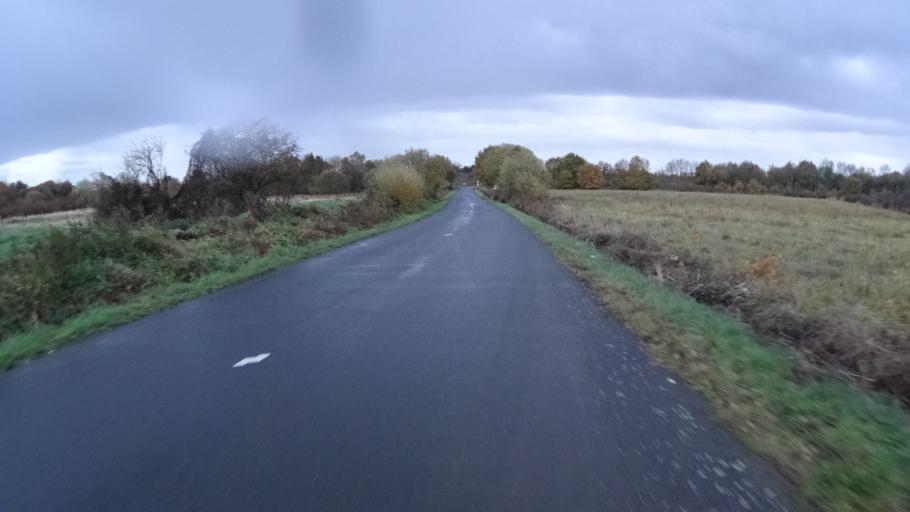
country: FR
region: Brittany
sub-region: Departement d'Ille-et-Vilaine
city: Sainte-Marie
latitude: 47.6813
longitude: -1.9941
